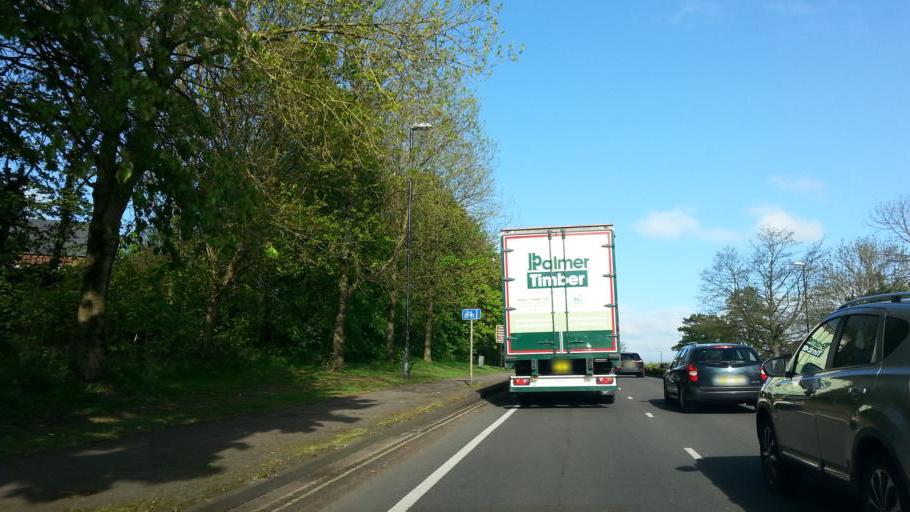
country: GB
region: England
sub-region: Warwickshire
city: Ryton on Dunsmore
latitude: 52.4051
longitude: -1.4627
